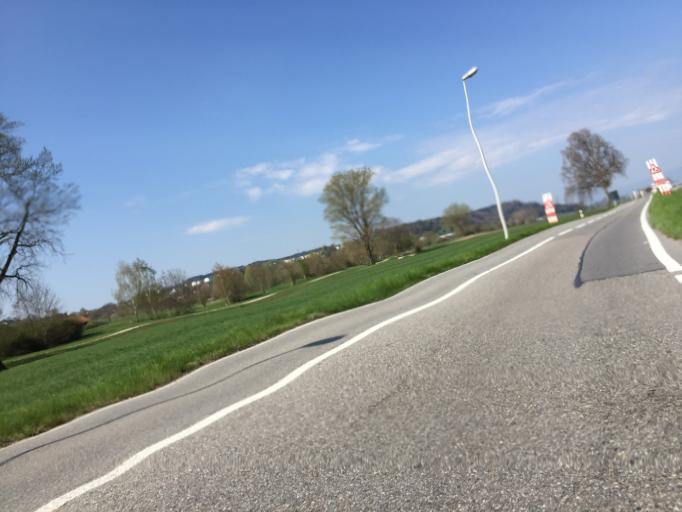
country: CH
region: Bern
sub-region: Bern-Mittelland District
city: Munchenbuchsee
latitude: 47.0296
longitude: 7.4594
